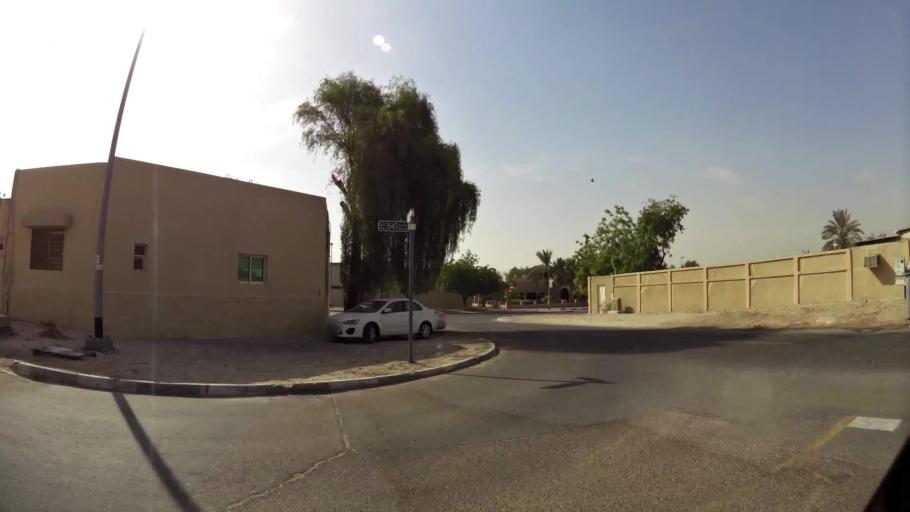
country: AE
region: Ash Shariqah
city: Sharjah
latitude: 25.2230
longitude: 55.3964
